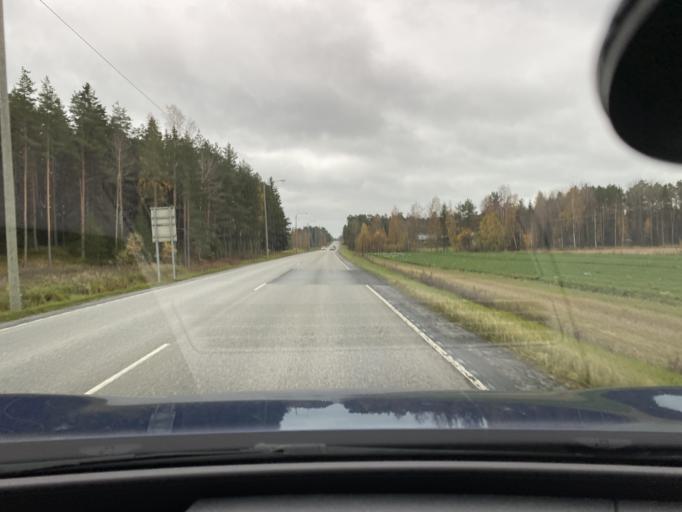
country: FI
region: Varsinais-Suomi
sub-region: Vakka-Suomi
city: Laitila
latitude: 60.9732
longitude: 21.5933
